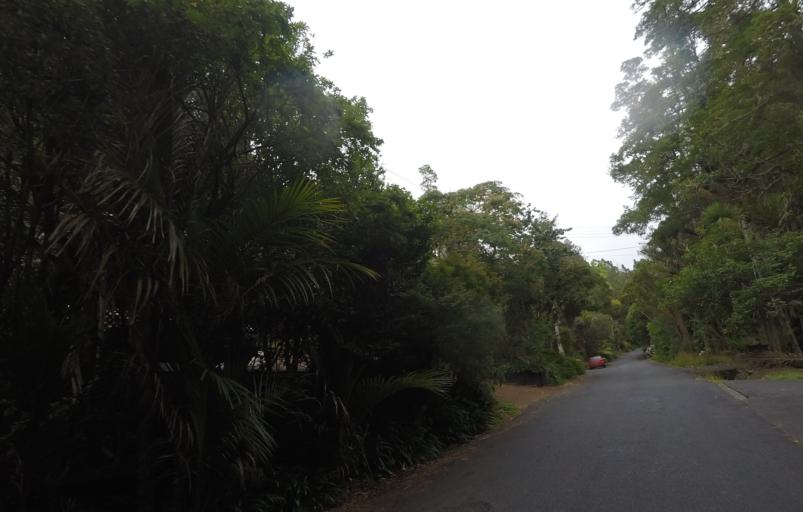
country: NZ
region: Auckland
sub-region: Auckland
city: Titirangi
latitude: -36.9478
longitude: 174.6632
